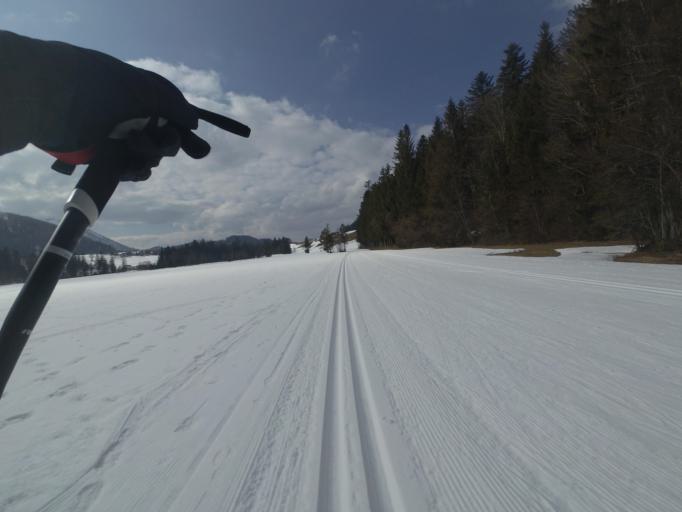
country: AT
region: Salzburg
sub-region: Politischer Bezirk Salzburg-Umgebung
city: Faistenau
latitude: 47.7684
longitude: 13.2641
